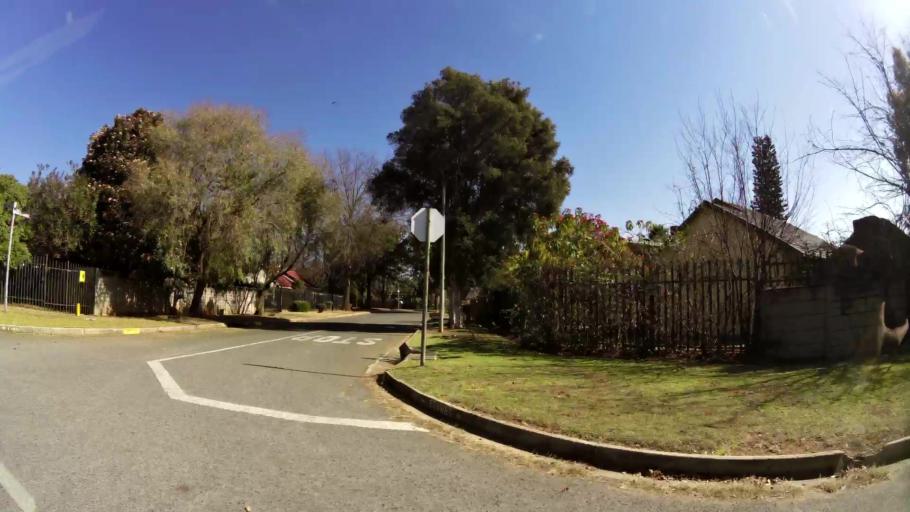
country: ZA
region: Gauteng
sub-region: City of Johannesburg Metropolitan Municipality
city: Modderfontein
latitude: -26.0625
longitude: 28.2141
